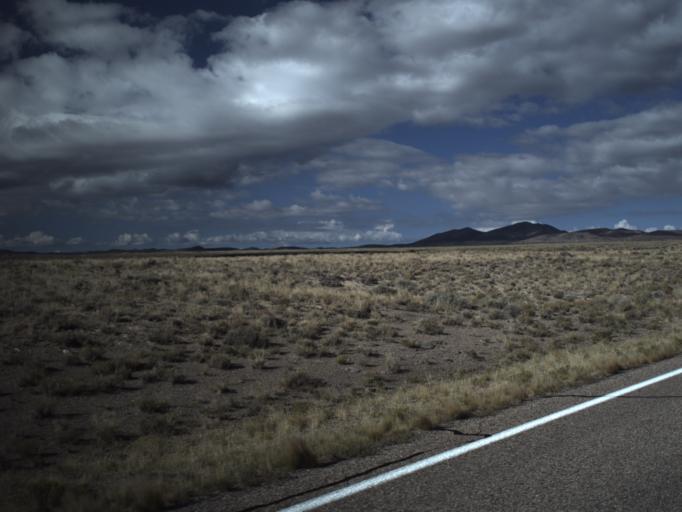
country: US
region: Utah
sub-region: Beaver County
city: Milford
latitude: 38.4406
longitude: -113.1620
